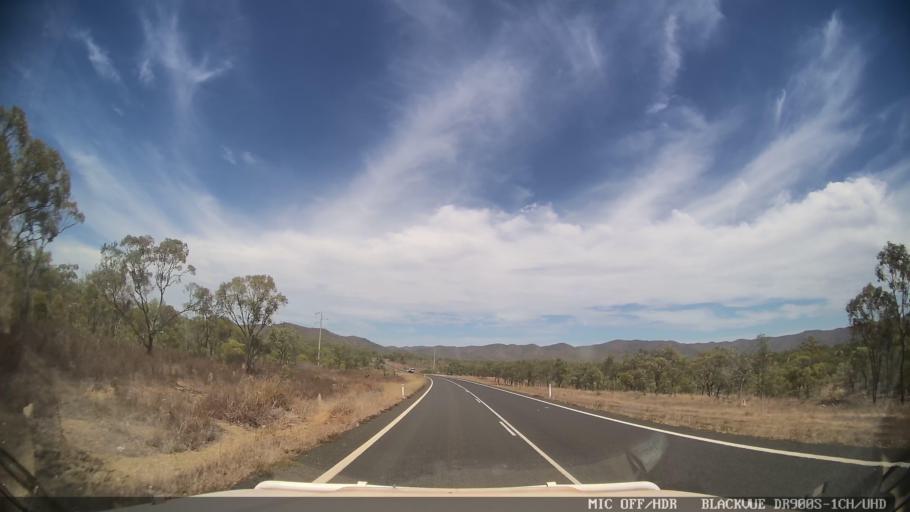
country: AU
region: Queensland
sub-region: Cook
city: Cooktown
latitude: -15.9240
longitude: 144.8415
